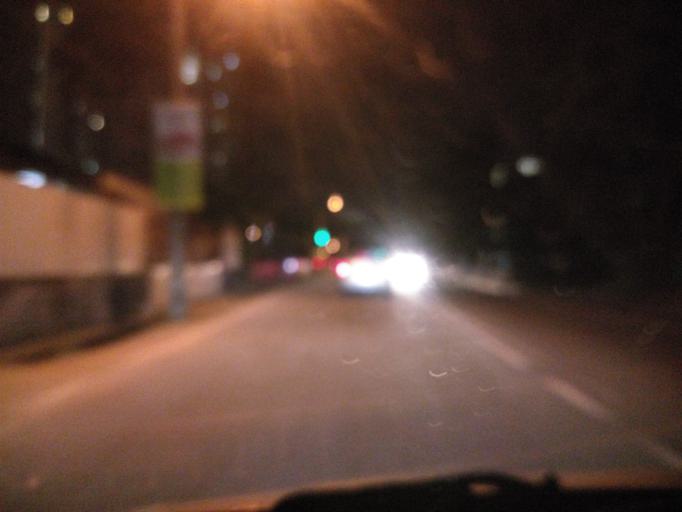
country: MY
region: Penang
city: Butterworth
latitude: 5.4020
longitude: 100.3748
